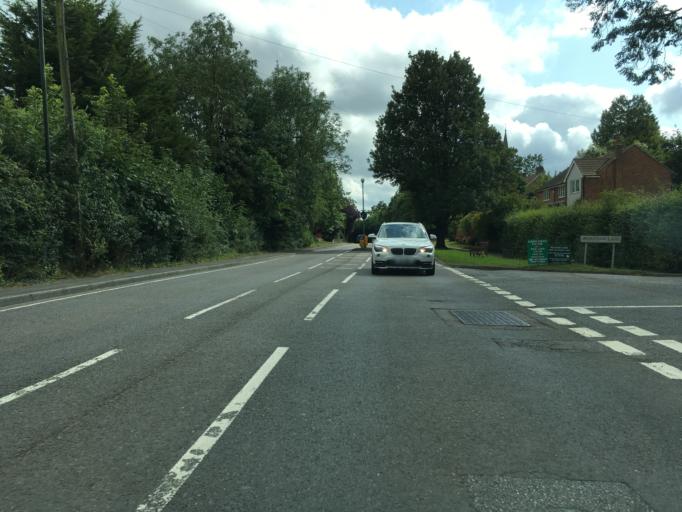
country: GB
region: England
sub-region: Kent
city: Tenterden
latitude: 51.0885
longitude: 0.6905
